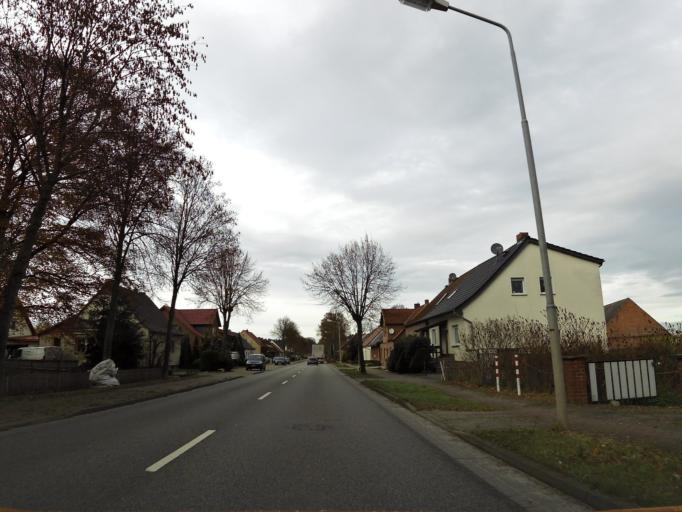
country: DE
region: Saxony-Anhalt
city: Kalbe
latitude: 52.6732
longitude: 11.2759
